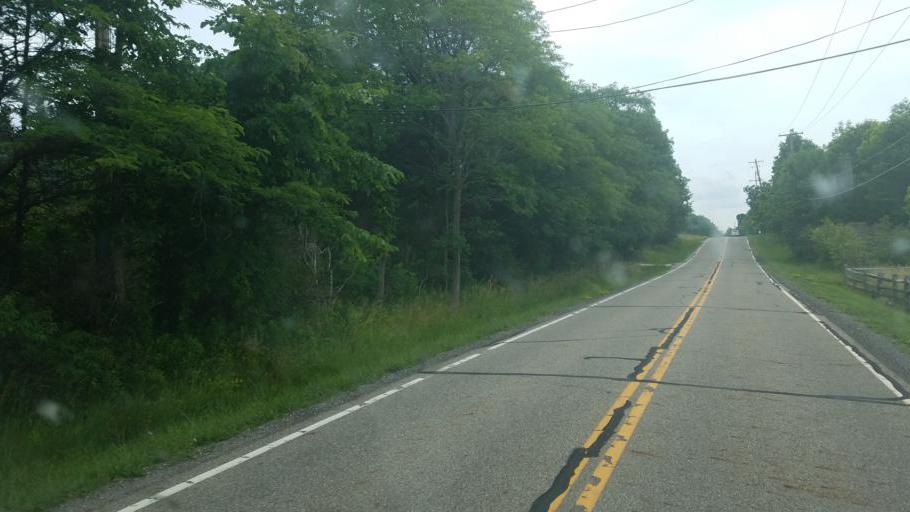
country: US
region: Ohio
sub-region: Geauga County
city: Burton
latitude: 41.4971
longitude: -81.1557
